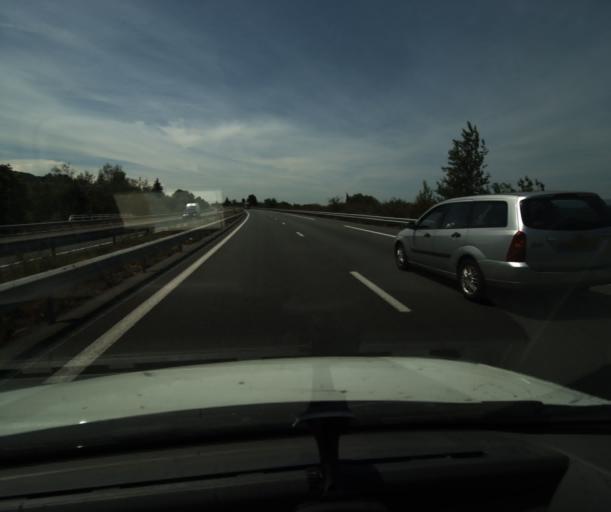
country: FR
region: Languedoc-Roussillon
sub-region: Departement de l'Aude
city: Capendu
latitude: 43.1821
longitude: 2.5214
